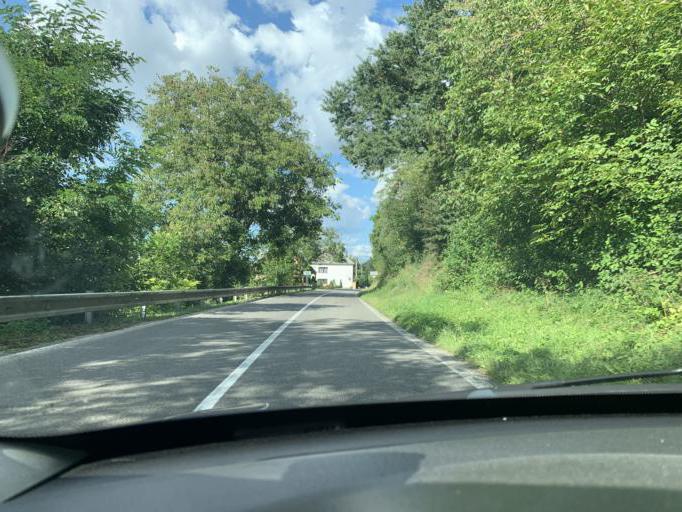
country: SK
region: Trenciansky
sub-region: Okres Nove Mesto nad Vahom
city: Nove Mesto nad Vahom
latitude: 48.8207
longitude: 17.9383
